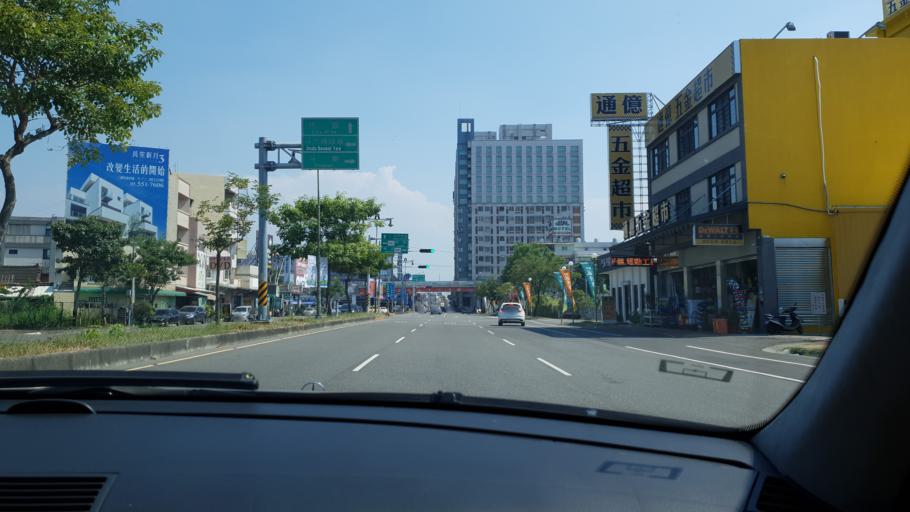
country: TW
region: Taiwan
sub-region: Yunlin
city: Douliu
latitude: 23.7146
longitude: 120.5318
